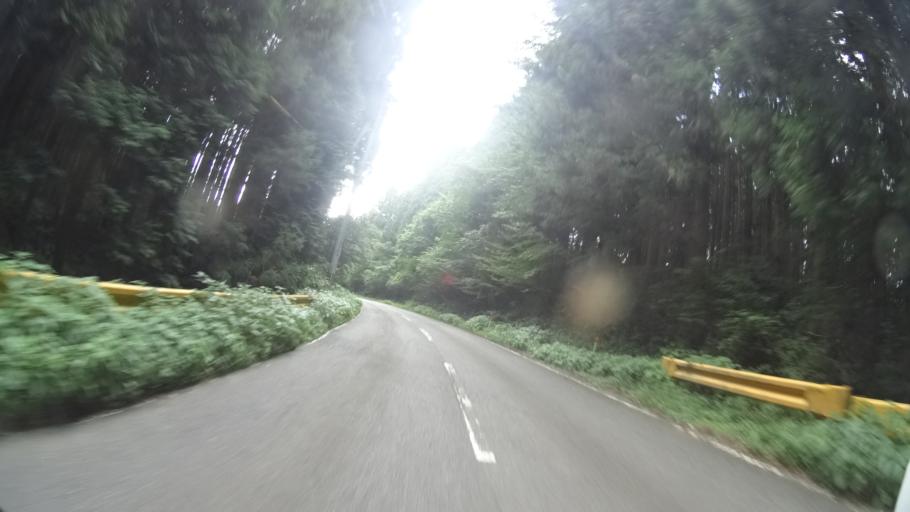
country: JP
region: Yamaguchi
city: Hagi
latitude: 34.5067
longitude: 131.5860
